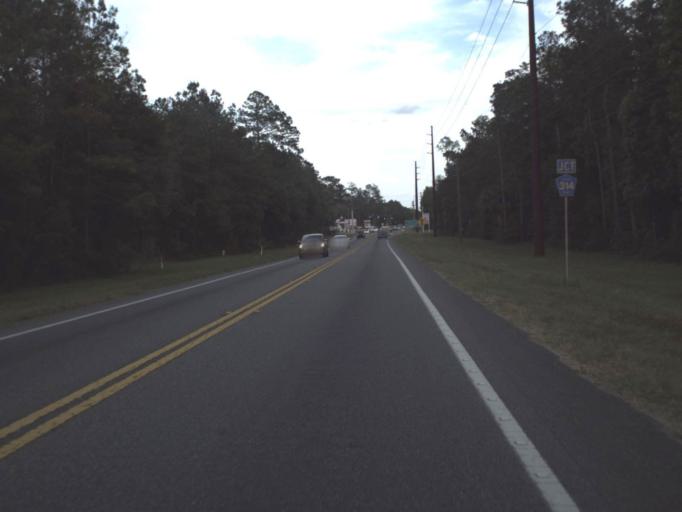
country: US
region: Florida
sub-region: Marion County
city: Silver Springs Shores
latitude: 29.2140
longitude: -81.9791
